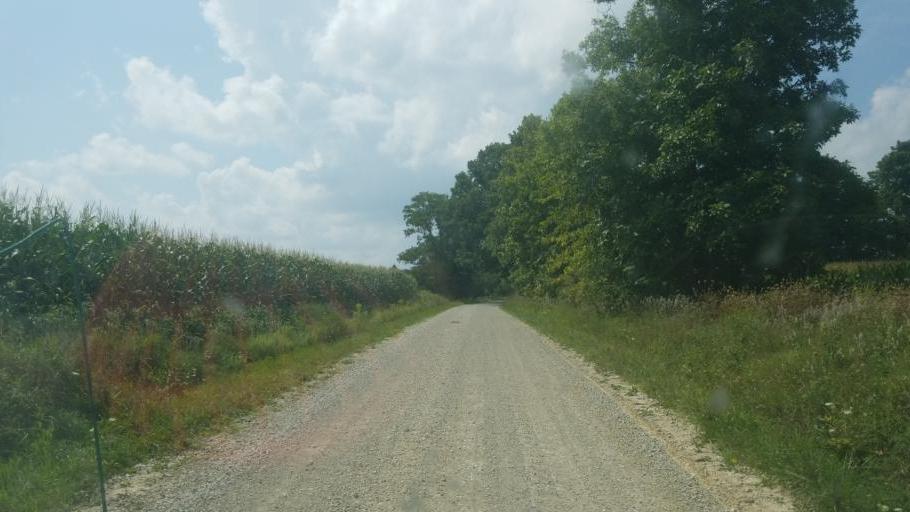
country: US
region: Ohio
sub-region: Huron County
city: New London
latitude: 40.9862
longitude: -82.4120
